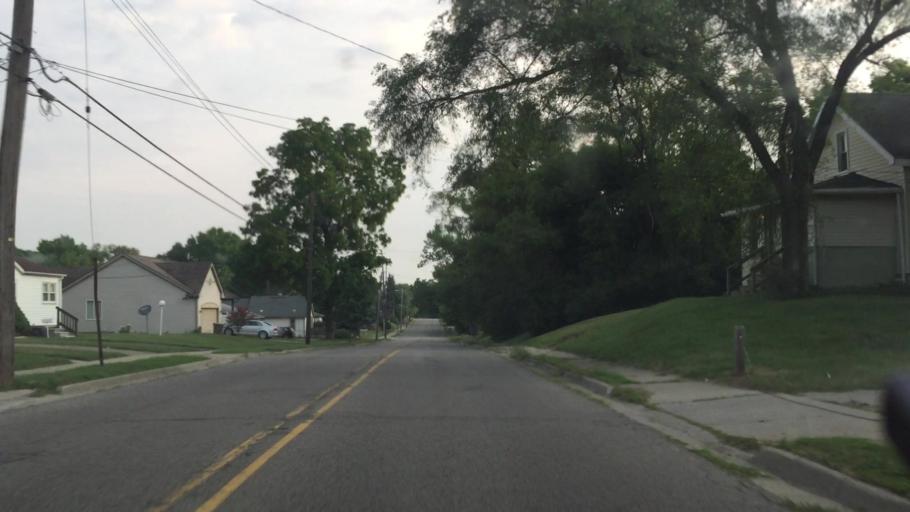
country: US
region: Michigan
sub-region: Oakland County
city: Pontiac
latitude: 42.6313
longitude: -83.2753
